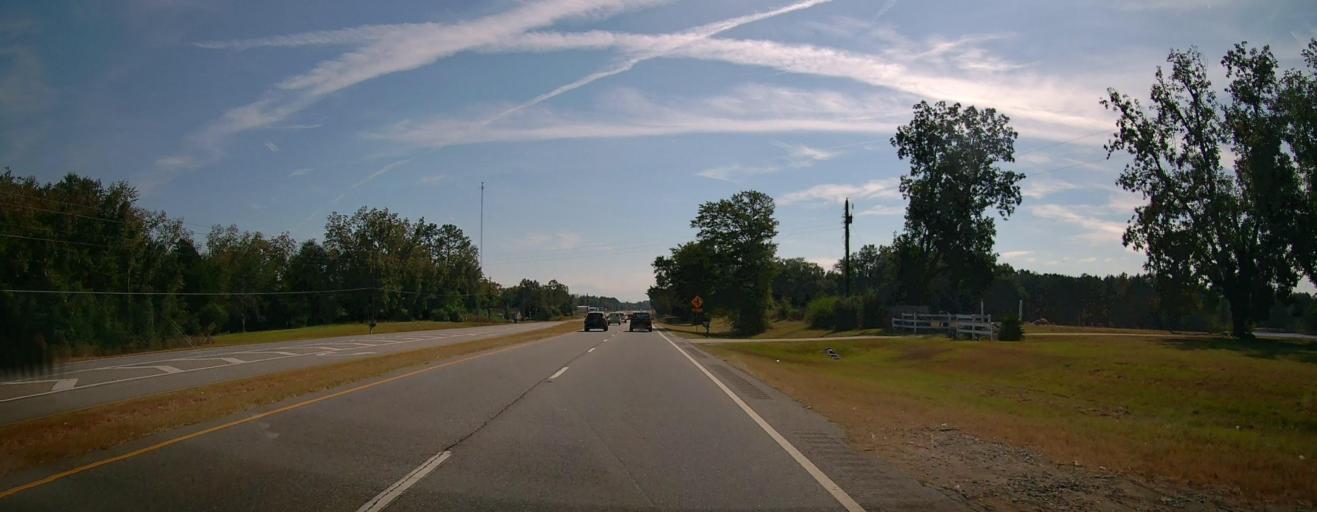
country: US
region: Georgia
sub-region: Dougherty County
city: Putney
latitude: 31.5071
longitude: -84.1156
